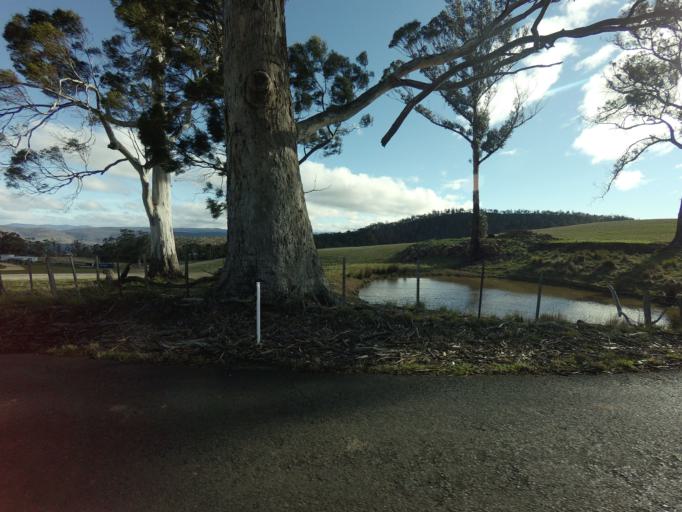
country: AU
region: Tasmania
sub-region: Derwent Valley
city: New Norfolk
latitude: -42.7234
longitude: 147.0328
